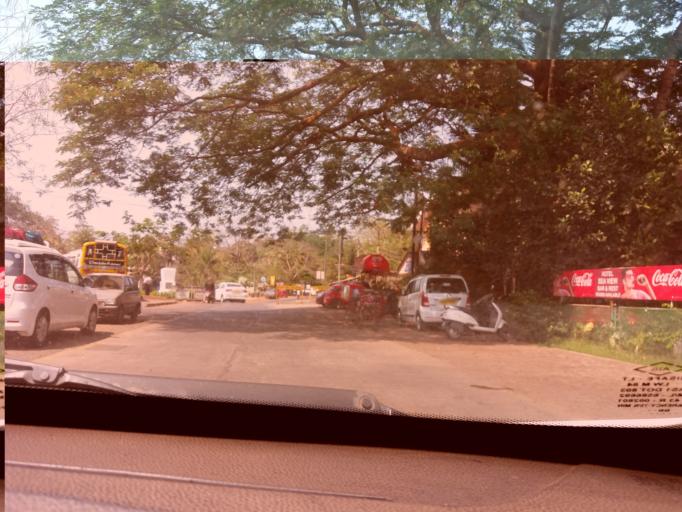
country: IN
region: Goa
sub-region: North Goa
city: Taleigao
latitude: 15.4568
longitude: 73.8033
